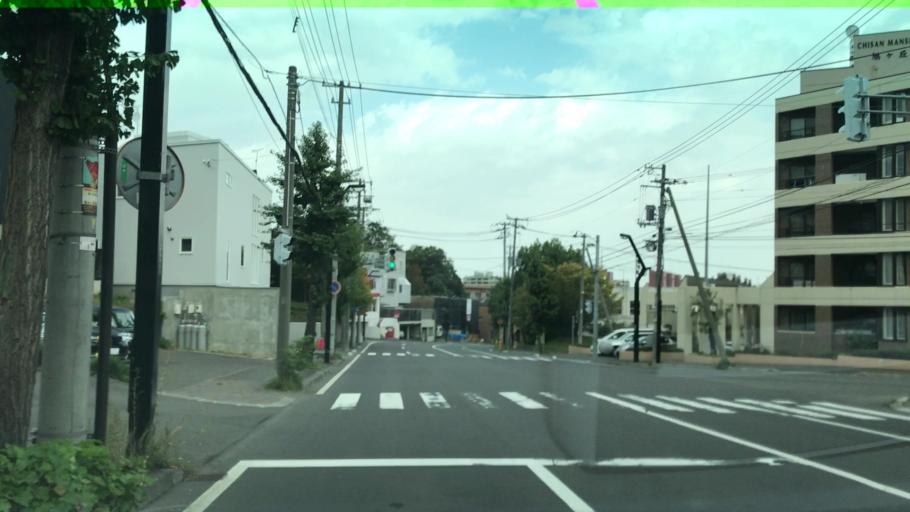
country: JP
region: Hokkaido
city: Sapporo
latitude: 43.0435
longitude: 141.3193
